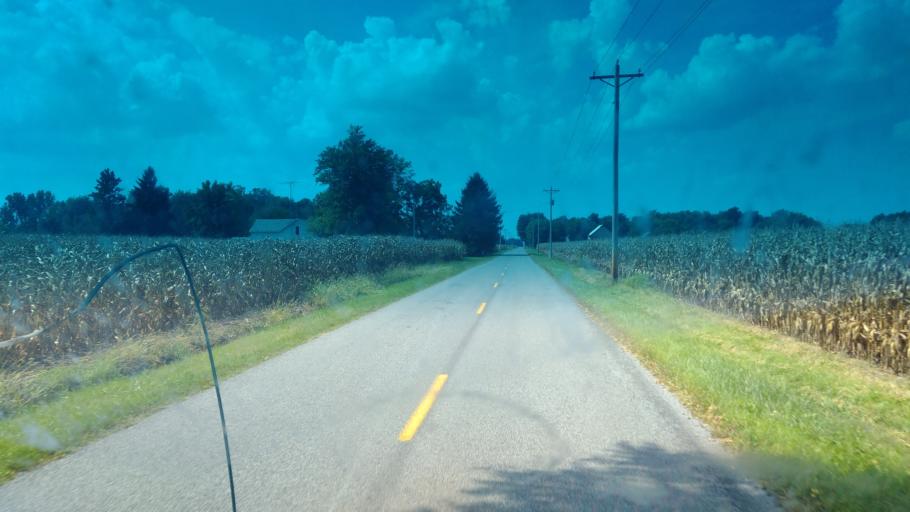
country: US
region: Ohio
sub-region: Hardin County
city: Ada
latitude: 40.7032
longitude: -83.8841
